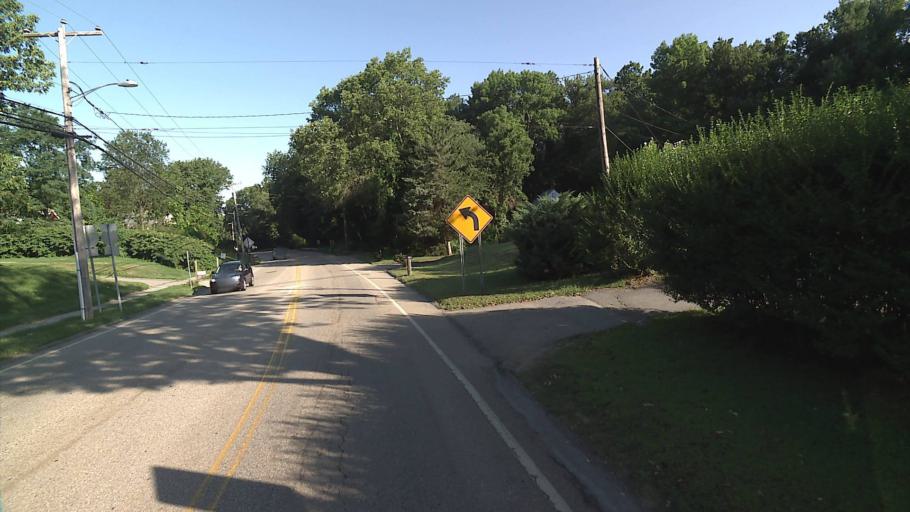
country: US
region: Connecticut
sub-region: New London County
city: Central Waterford
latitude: 41.3549
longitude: -72.1653
